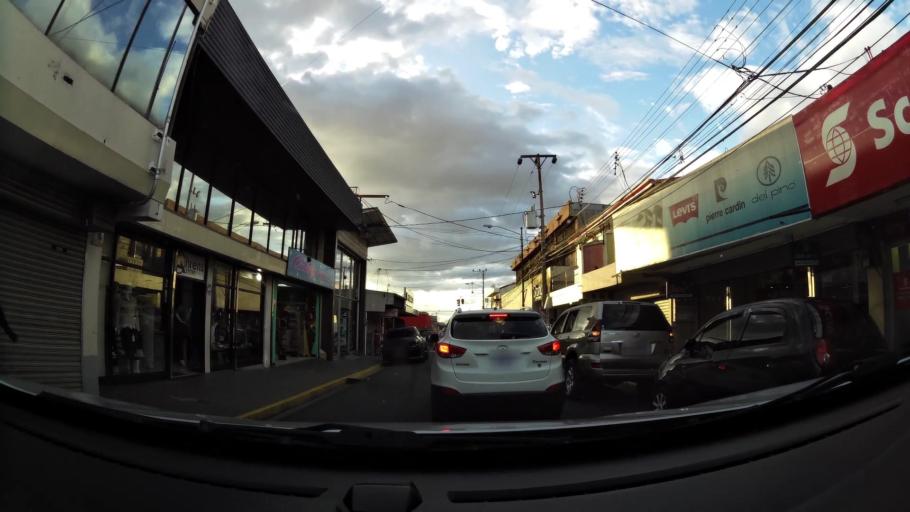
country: CR
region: Heredia
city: Heredia
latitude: 9.9972
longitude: -84.1171
